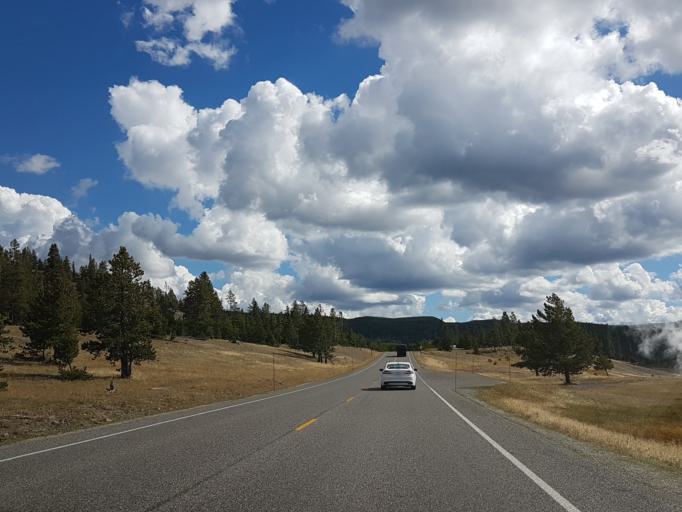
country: US
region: Montana
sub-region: Gallatin County
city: West Yellowstone
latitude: 44.5239
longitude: -110.8311
